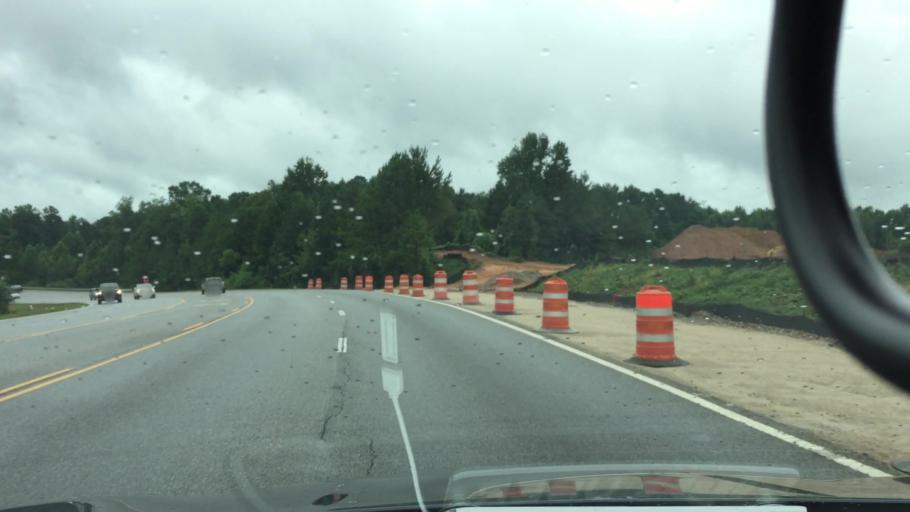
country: US
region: Alabama
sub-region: Lee County
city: Auburn
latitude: 32.6041
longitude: -85.4392
